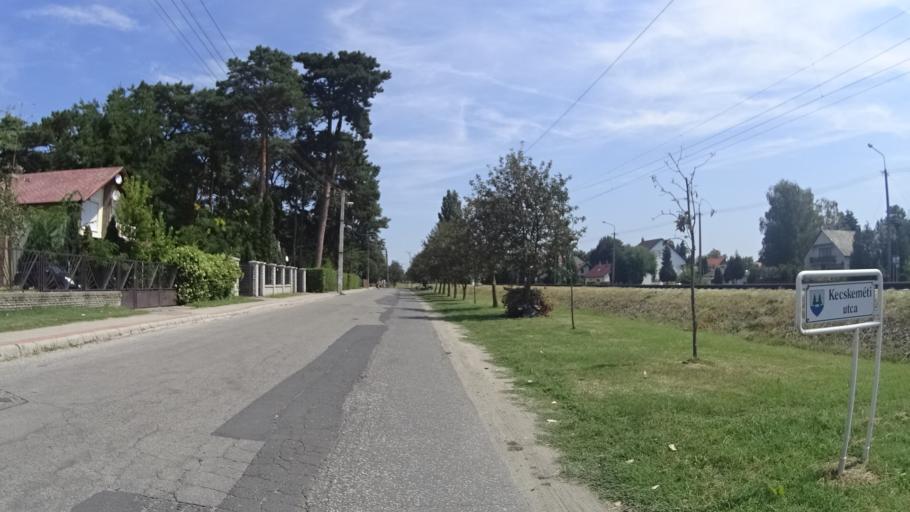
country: HU
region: Somogy
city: Balatonfenyves
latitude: 46.7158
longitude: 17.4943
